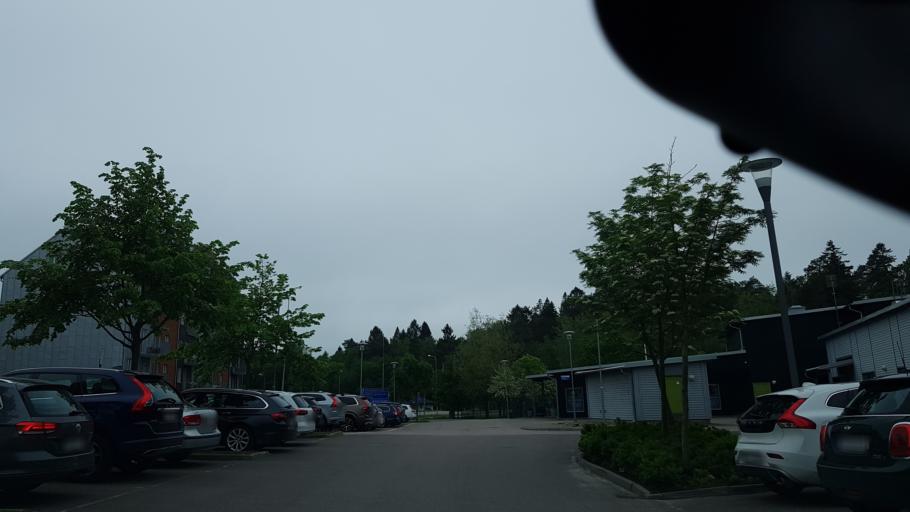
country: SE
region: Vaestra Goetaland
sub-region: Goteborg
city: Billdal
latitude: 57.6003
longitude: 11.9473
